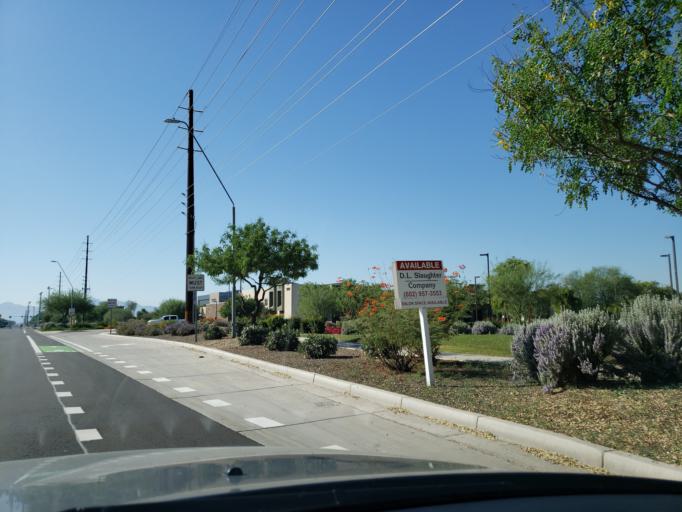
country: US
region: Arizona
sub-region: Maricopa County
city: Tolleson
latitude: 33.4829
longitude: -112.2553
